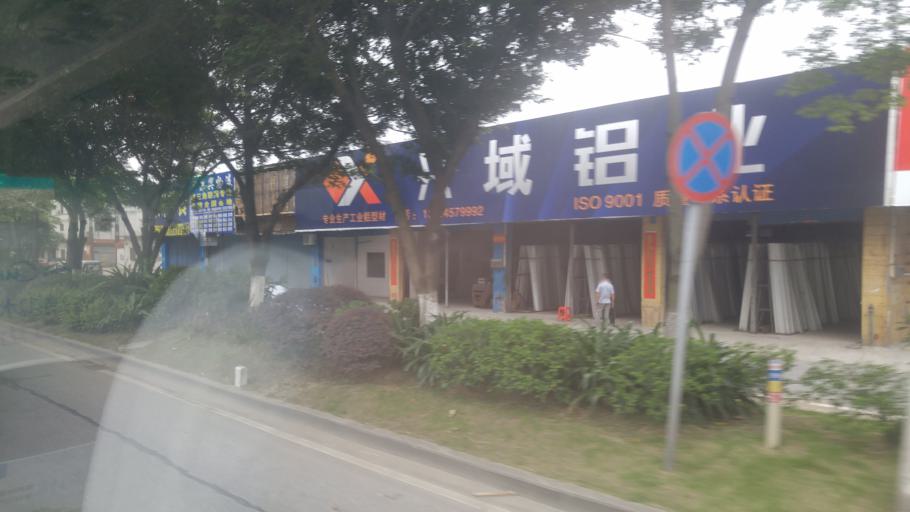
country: CN
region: Guangdong
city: Dali
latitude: 23.1037
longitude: 113.1365
